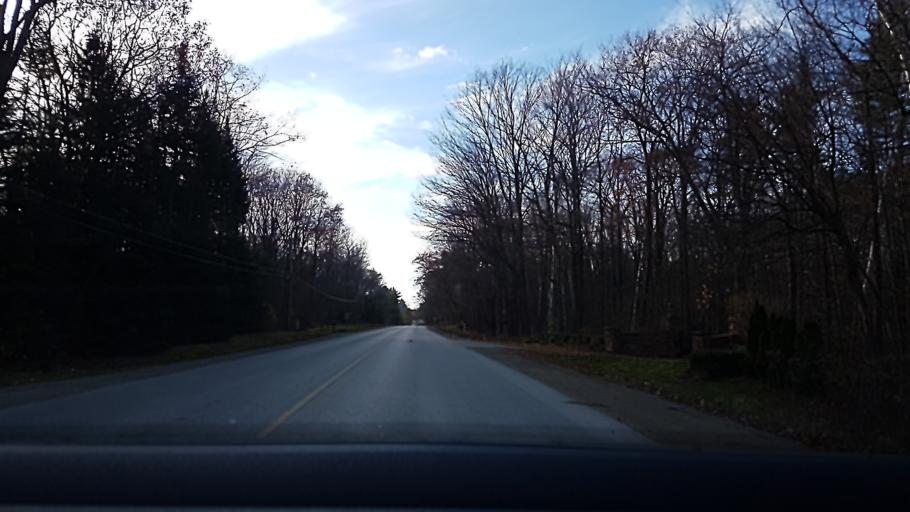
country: CA
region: Ontario
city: Barrie
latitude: 44.3926
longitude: -79.5472
